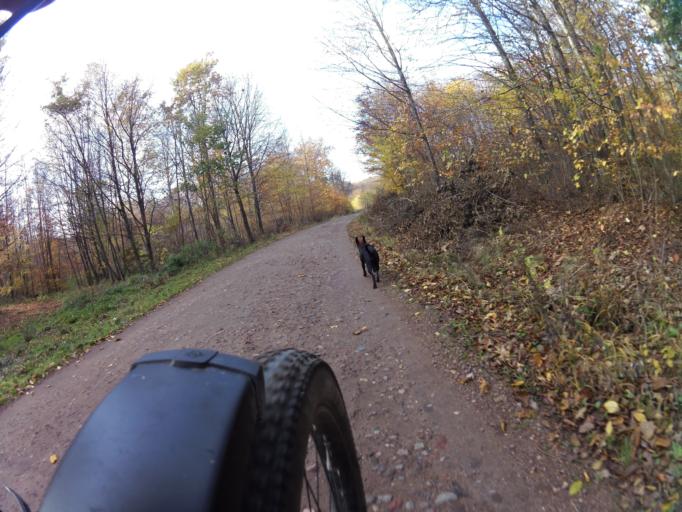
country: PL
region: Pomeranian Voivodeship
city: Strzelno
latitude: 54.7403
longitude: 18.2568
